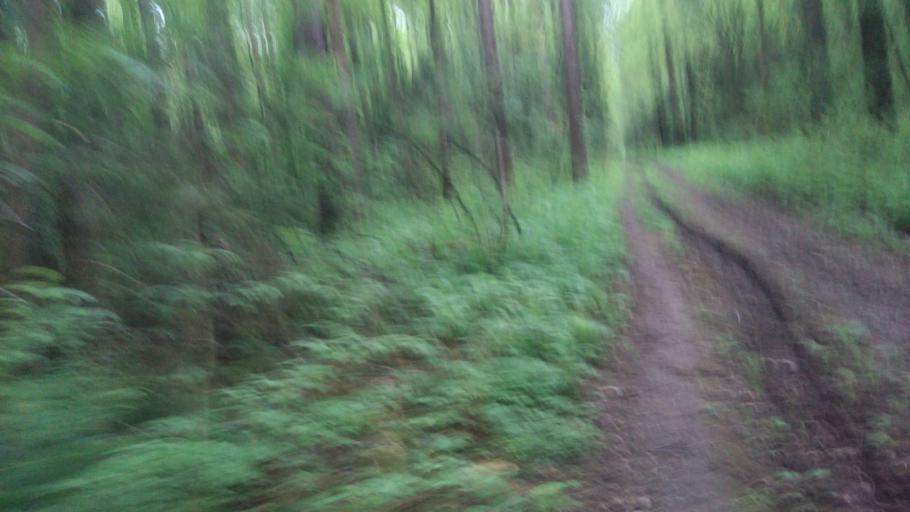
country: RU
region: Perm
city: Froly
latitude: 57.9624
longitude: 56.2987
